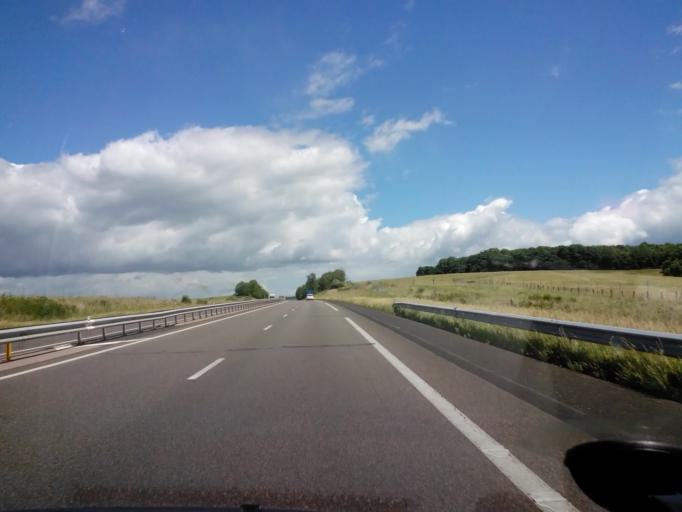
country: FR
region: Lorraine
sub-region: Departement des Vosges
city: Bulgneville
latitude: 48.1971
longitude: 5.7861
